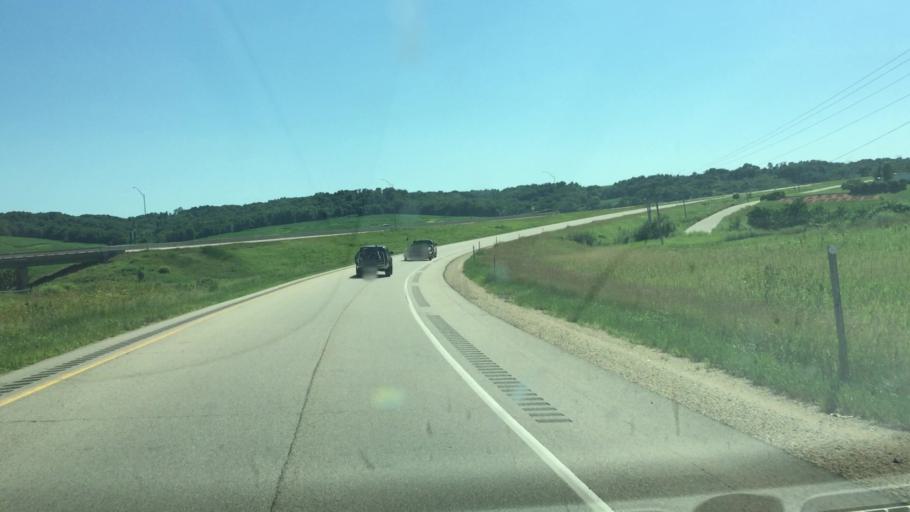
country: US
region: Iowa
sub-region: Dubuque County
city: Dubuque
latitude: 42.4212
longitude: -90.6946
